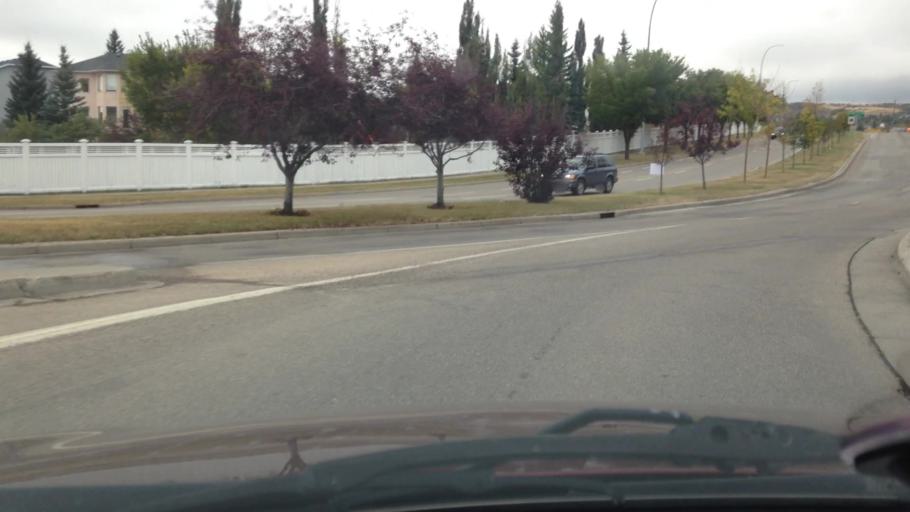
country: CA
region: Alberta
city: Calgary
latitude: 51.1463
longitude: -114.1064
